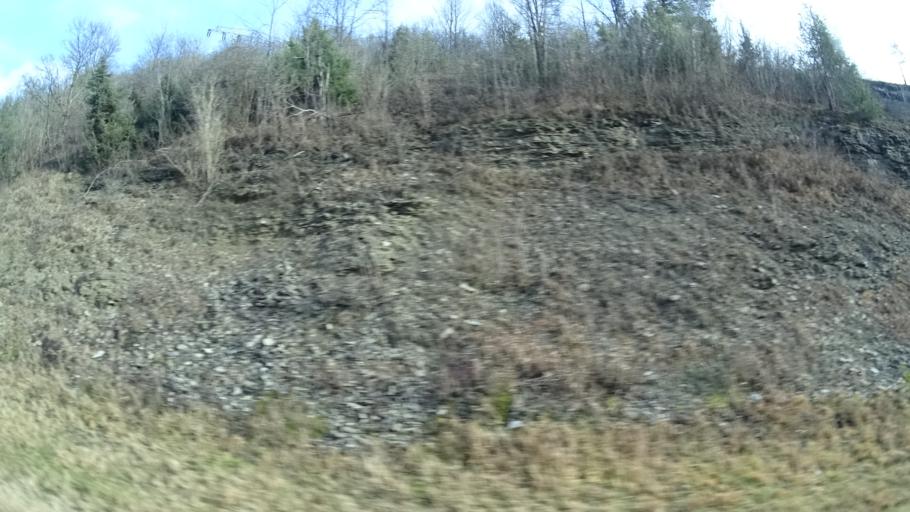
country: DE
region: Thuringia
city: Utendorf
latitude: 50.6029
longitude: 10.4411
